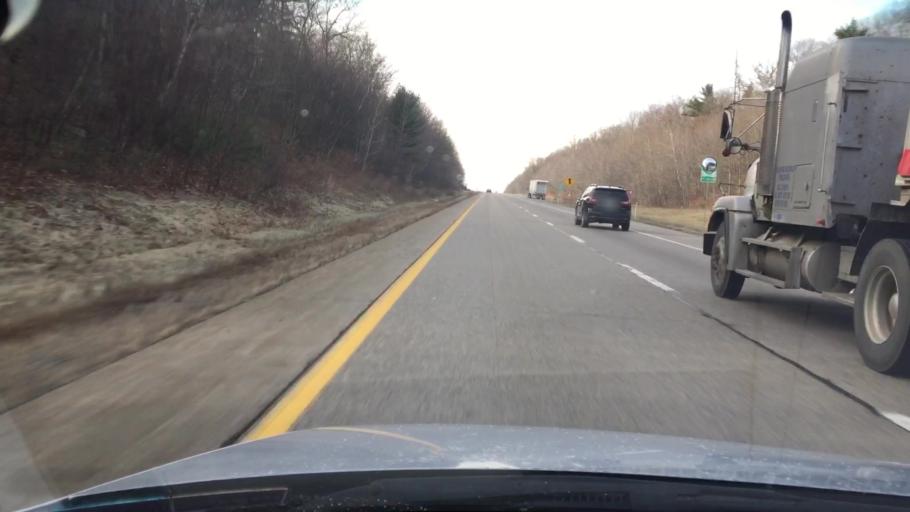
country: US
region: Pennsylvania
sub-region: Luzerne County
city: Conyngham
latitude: 41.0463
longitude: -76.0150
